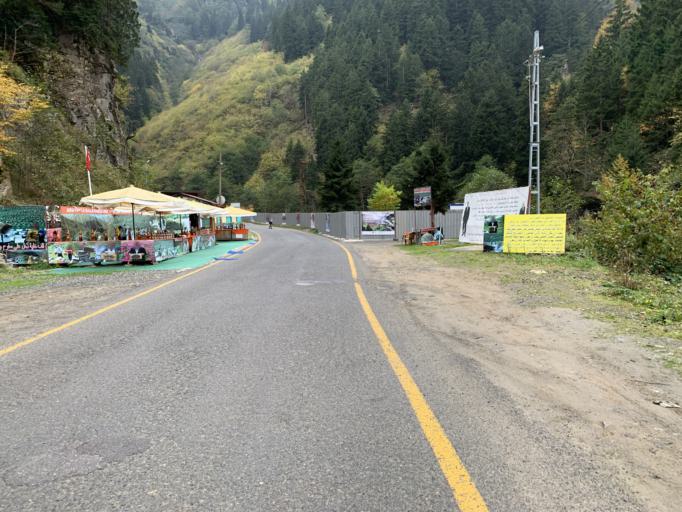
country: TR
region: Trabzon
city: Uzungol
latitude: 40.5952
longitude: 40.3210
